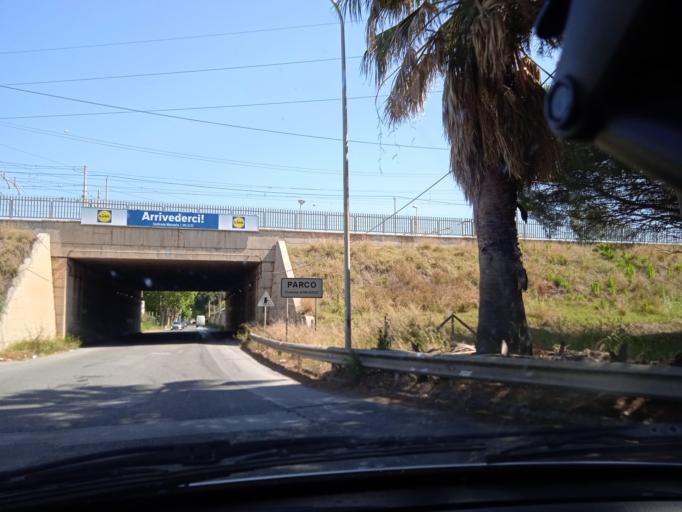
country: IT
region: Sicily
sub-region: Messina
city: Milazzo
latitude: 38.1980
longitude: 15.2526
